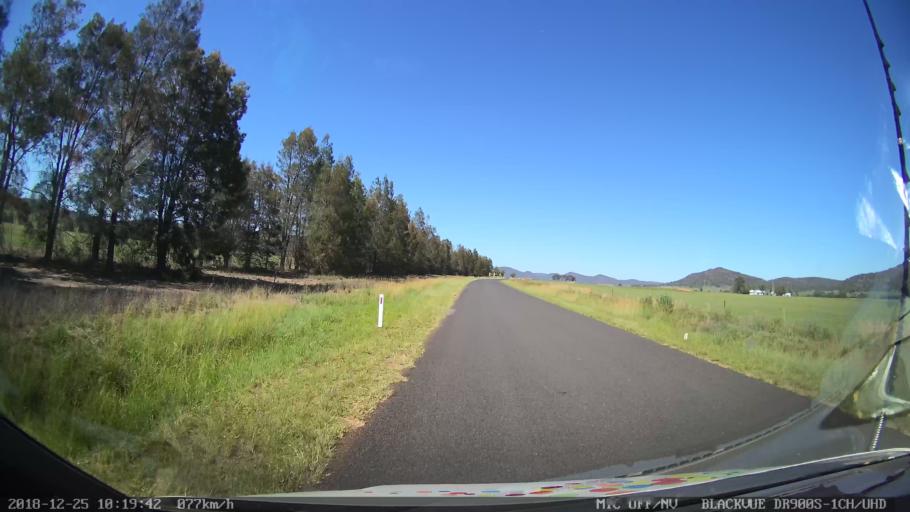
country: AU
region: New South Wales
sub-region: Muswellbrook
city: Denman
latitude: -32.3533
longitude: 150.5564
